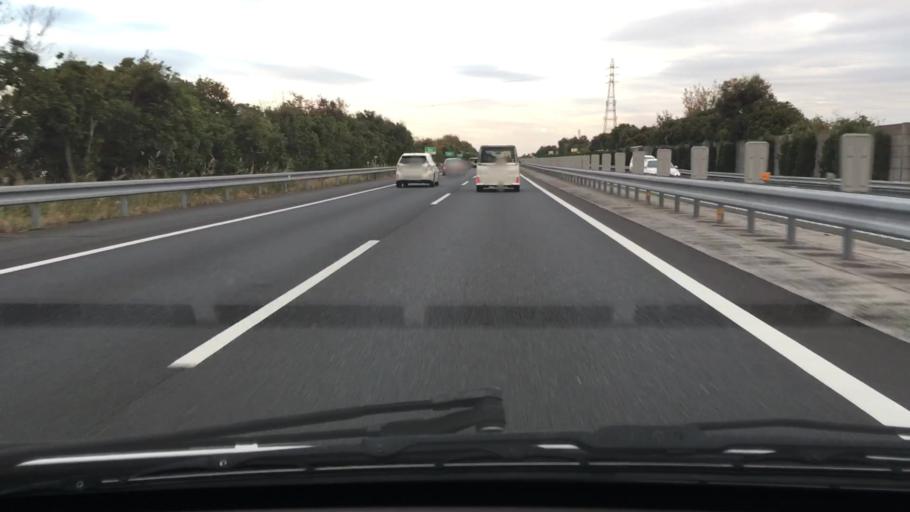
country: JP
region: Chiba
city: Ichihara
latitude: 35.5209
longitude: 140.1226
